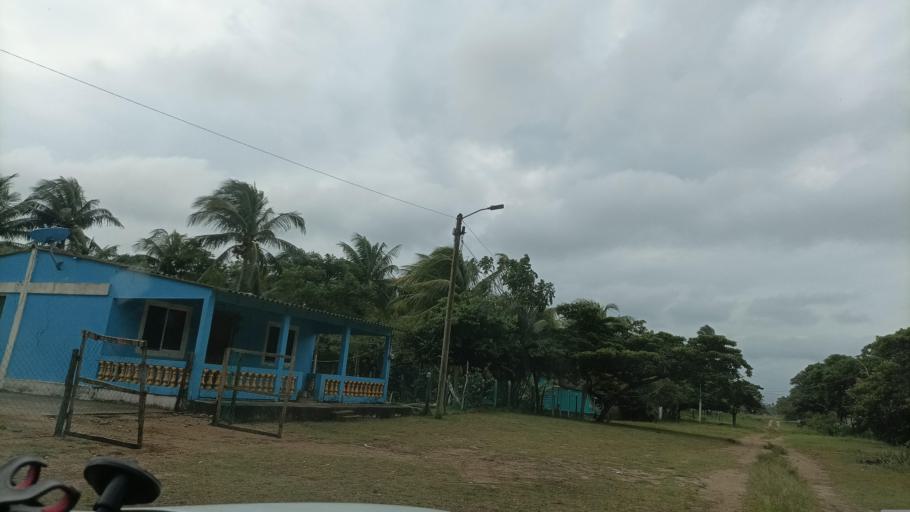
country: MX
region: Veracruz
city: Agua Dulce
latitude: 18.2086
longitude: -94.1421
